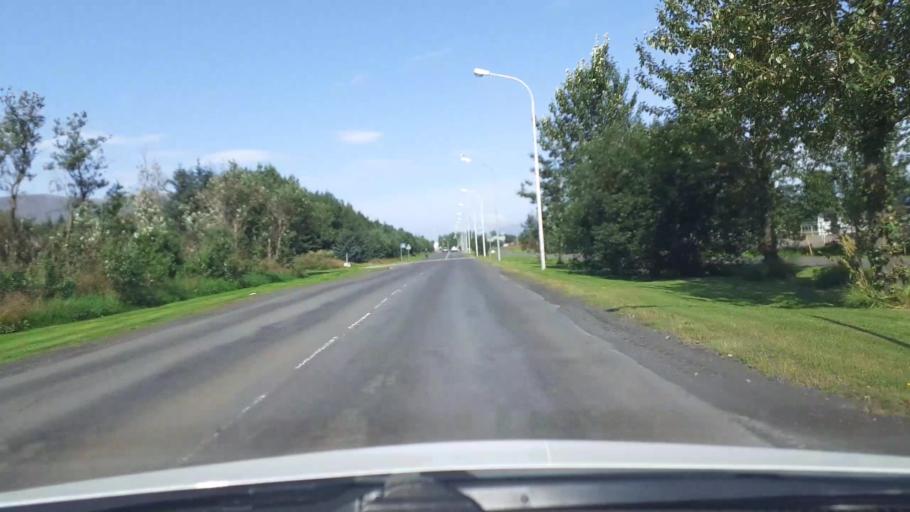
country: IS
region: South
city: Selfoss
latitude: 63.9330
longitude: -20.9791
